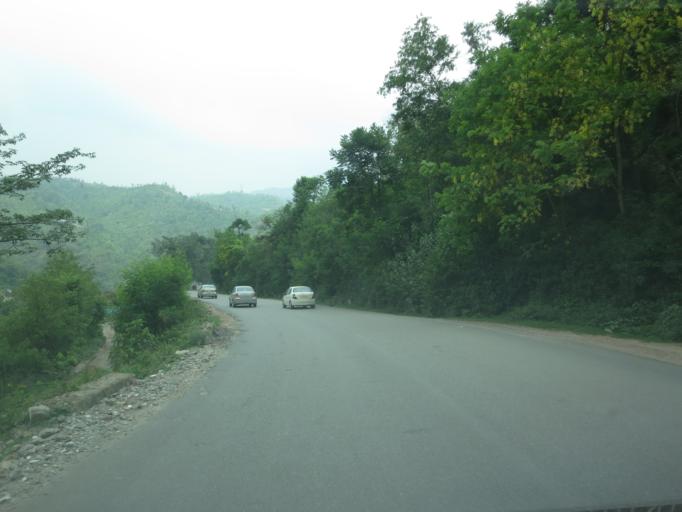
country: IN
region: Himachal Pradesh
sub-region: Mandi
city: Sundarnagar
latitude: 31.4460
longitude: 76.8558
